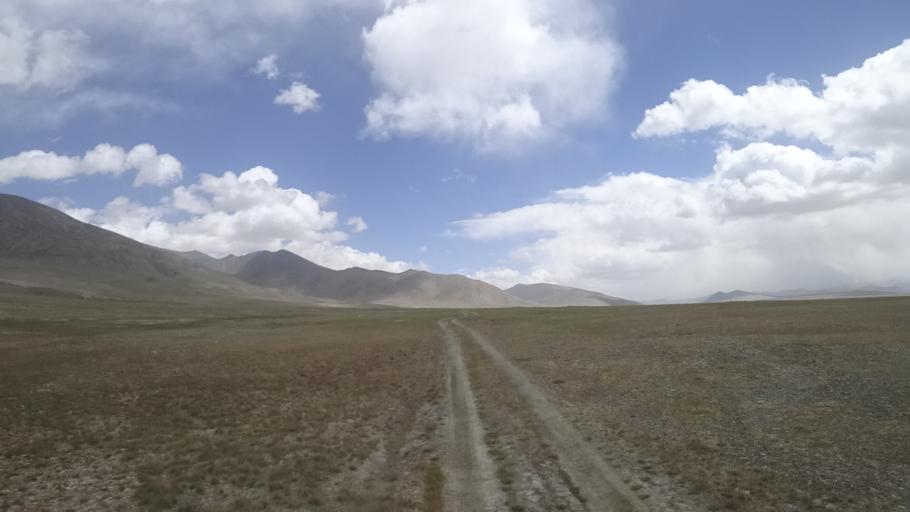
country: TJ
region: Gorno-Badakhshan
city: Murghob
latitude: 37.4842
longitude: 73.9853
